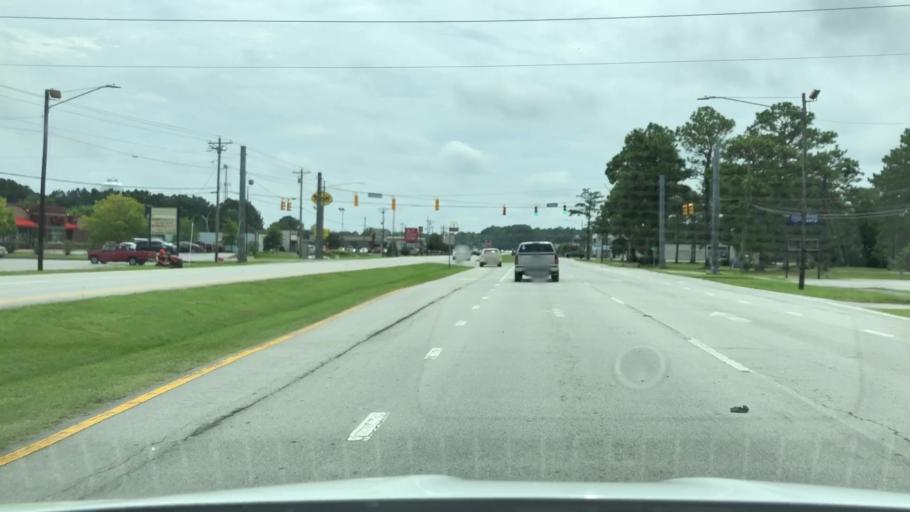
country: US
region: North Carolina
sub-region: Craven County
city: Havelock
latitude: 34.8642
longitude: -76.8986
